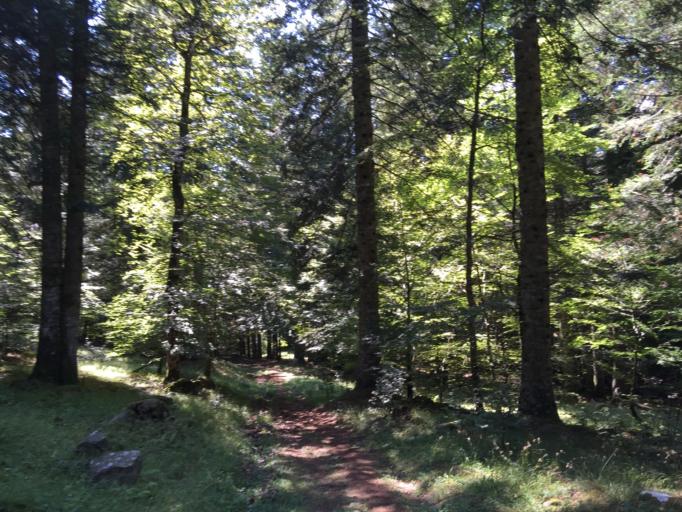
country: FR
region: Midi-Pyrenees
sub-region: Departement de l'Aveyron
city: Laguiole
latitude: 44.6448
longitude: 2.9254
